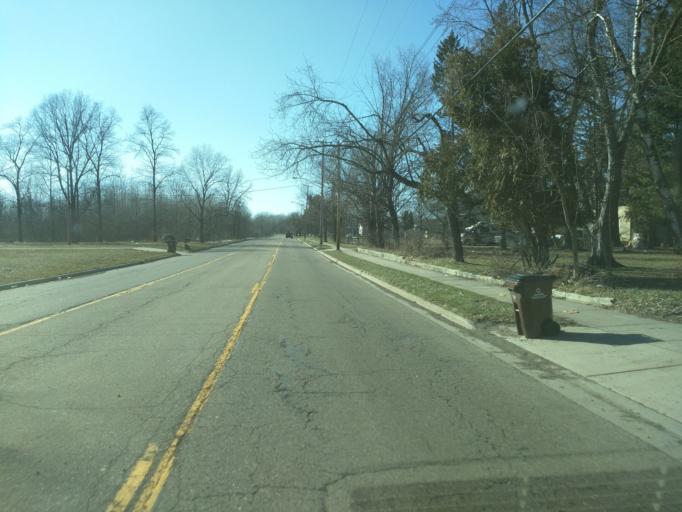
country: US
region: Michigan
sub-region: Eaton County
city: Dimondale
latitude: 42.6693
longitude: -84.5954
